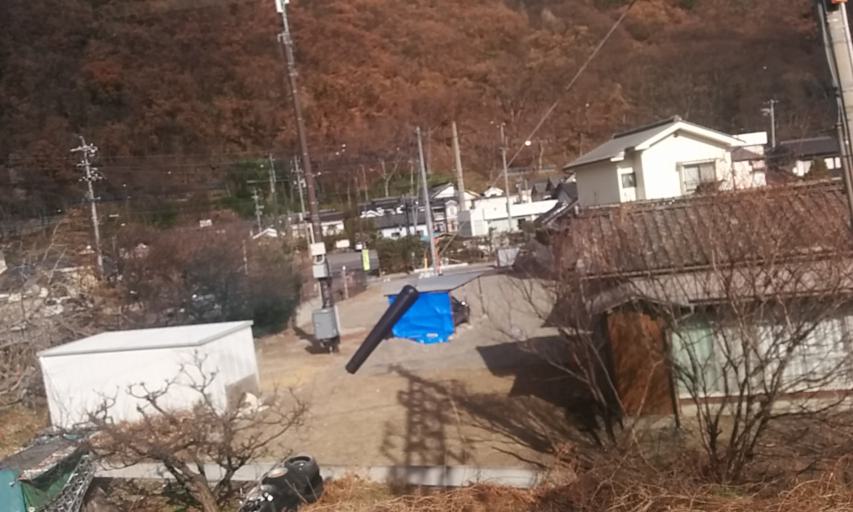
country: JP
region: Nagano
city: Ueda
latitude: 36.4184
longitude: 138.2054
